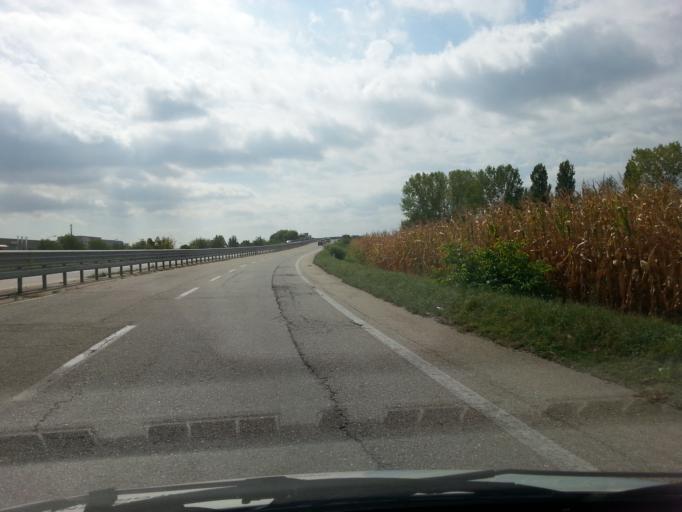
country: IT
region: Piedmont
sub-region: Provincia di Torino
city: Riva
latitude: 44.8999
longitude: 7.3607
